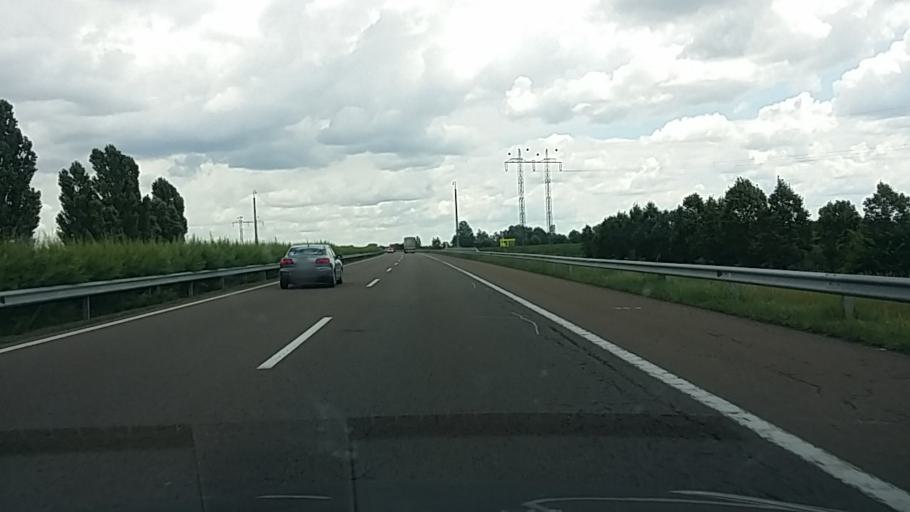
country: HU
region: Borsod-Abauj-Zemplen
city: Mezokeresztes
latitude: 47.8033
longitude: 20.6788
